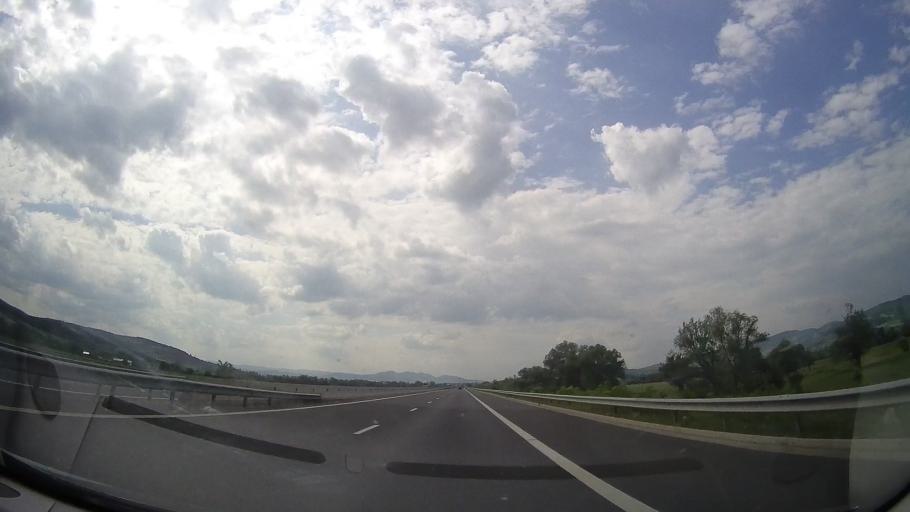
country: RO
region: Hunedoara
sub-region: Comuna Turdas
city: Turdas
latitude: 45.8385
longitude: 23.0938
